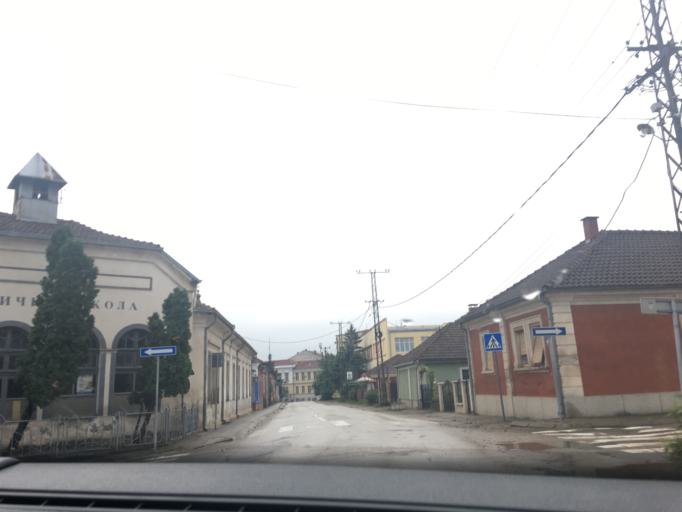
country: RS
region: Central Serbia
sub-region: Nisavski Okrug
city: Aleksinac
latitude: 43.5437
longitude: 21.7065
